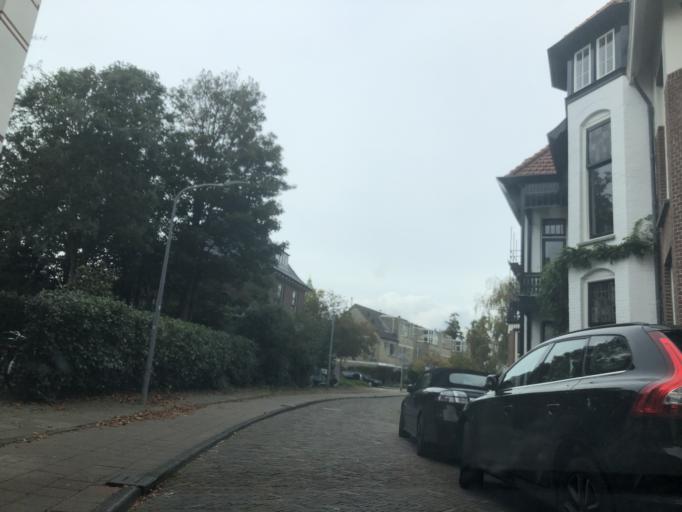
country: NL
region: North Holland
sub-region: Gemeente Haarlem
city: Haarlem
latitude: 52.3733
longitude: 4.6237
